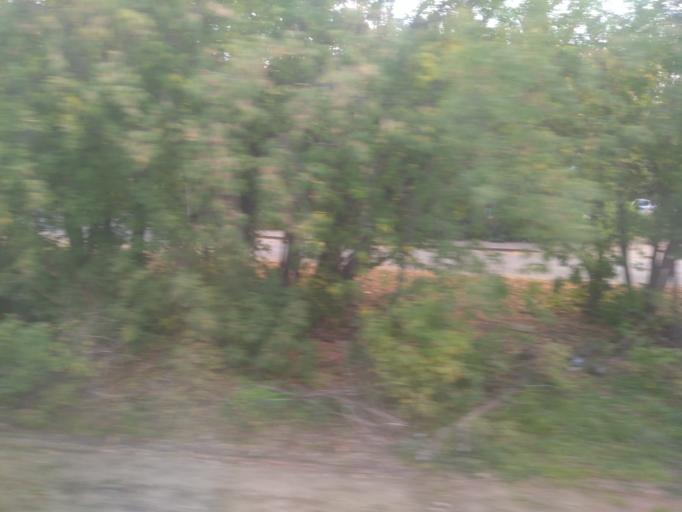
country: RU
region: Tatarstan
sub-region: Gorod Kazan'
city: Kazan
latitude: 55.8039
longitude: 49.0603
